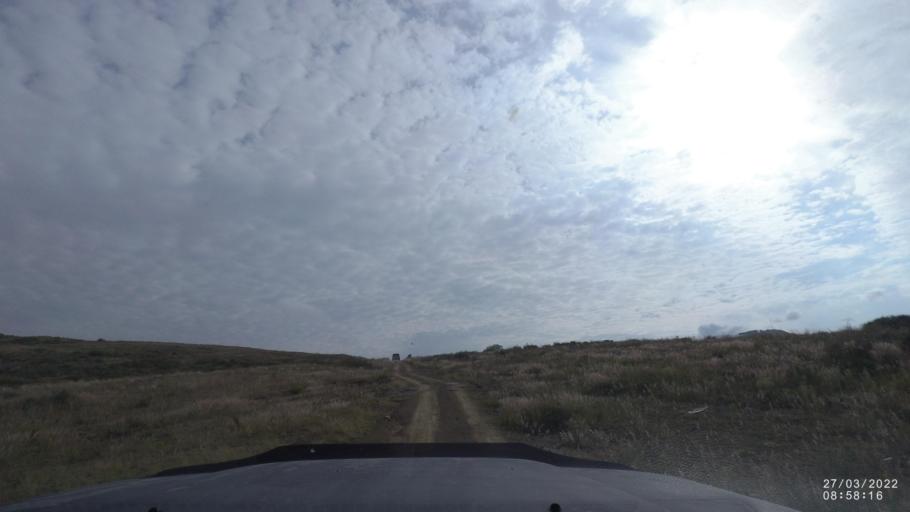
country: BO
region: Cochabamba
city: Cliza
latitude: -17.7434
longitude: -65.8572
